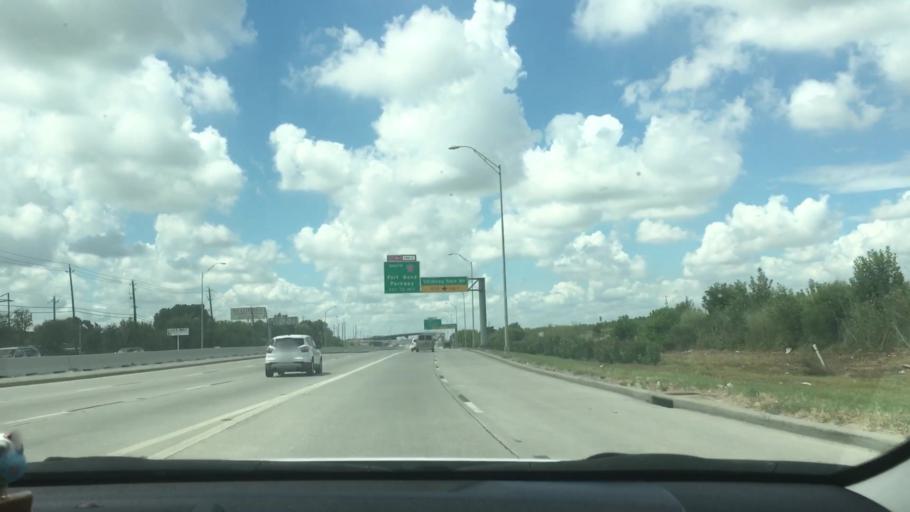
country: US
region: Texas
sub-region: Harris County
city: Bellaire
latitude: 29.6451
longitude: -95.4704
